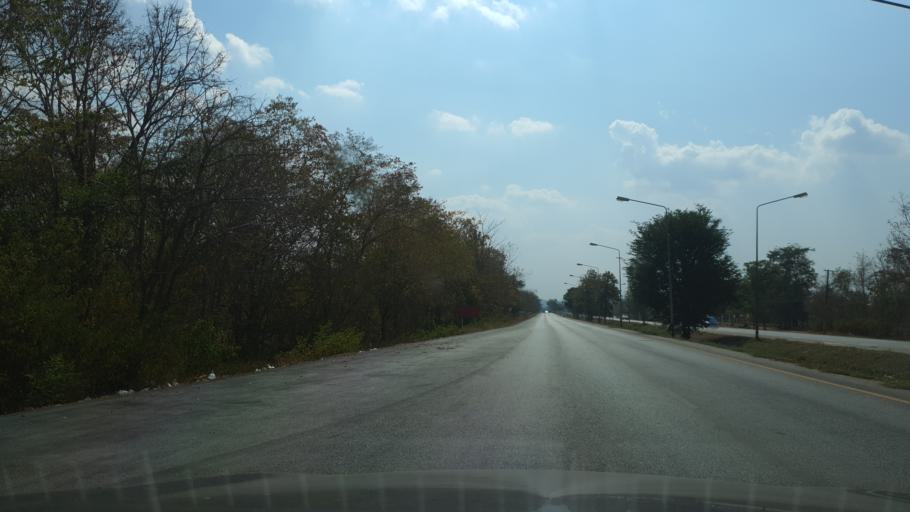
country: TH
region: Lampang
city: Mae Phrik
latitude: 17.4399
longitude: 99.1590
